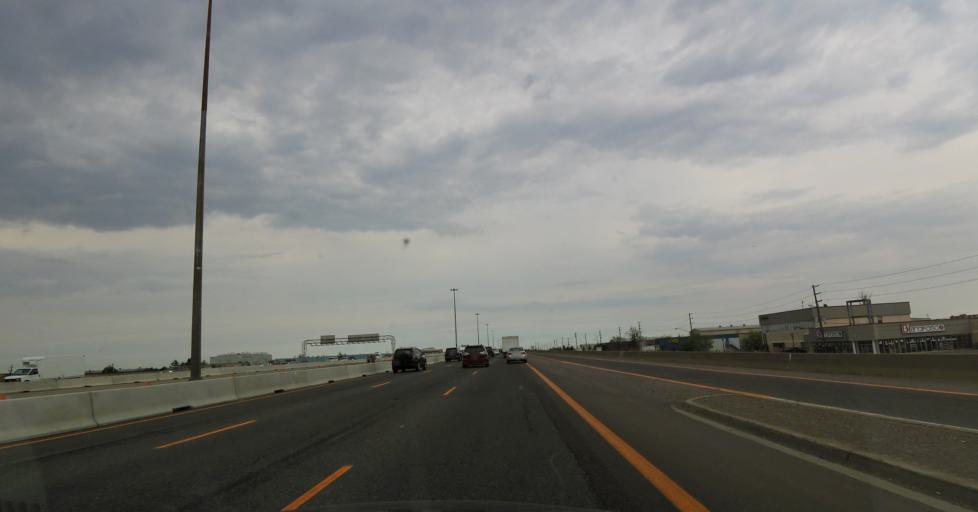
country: CA
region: Ontario
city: Brampton
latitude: 43.7004
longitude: -79.7317
